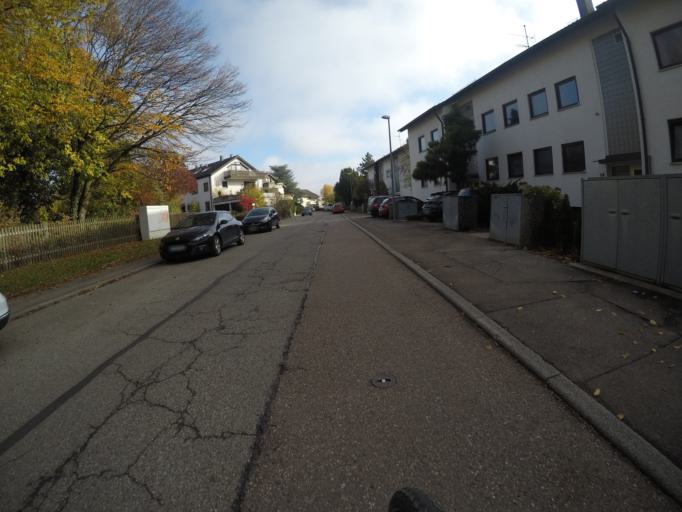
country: DE
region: Baden-Wuerttemberg
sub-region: Regierungsbezirk Stuttgart
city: Leinfelden-Echterdingen
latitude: 48.7201
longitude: 9.1503
